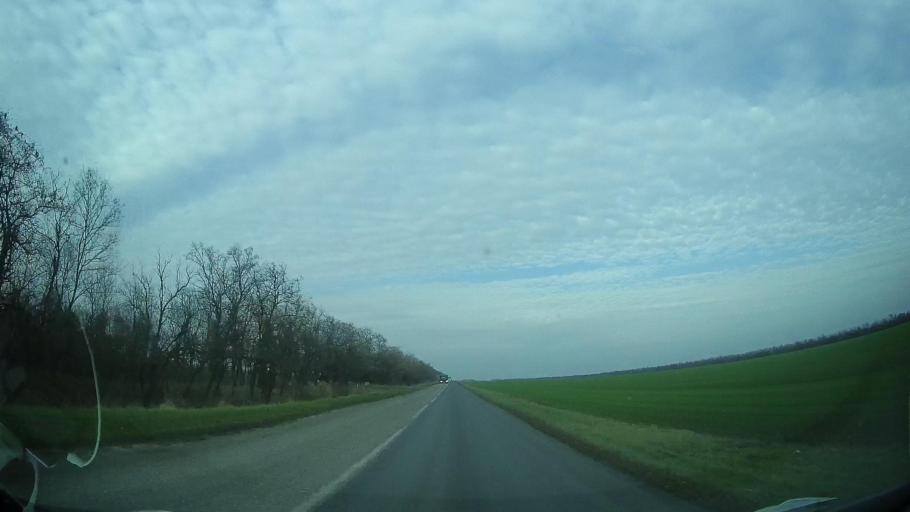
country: RU
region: Rostov
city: Zernograd
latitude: 46.9417
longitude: 40.3666
